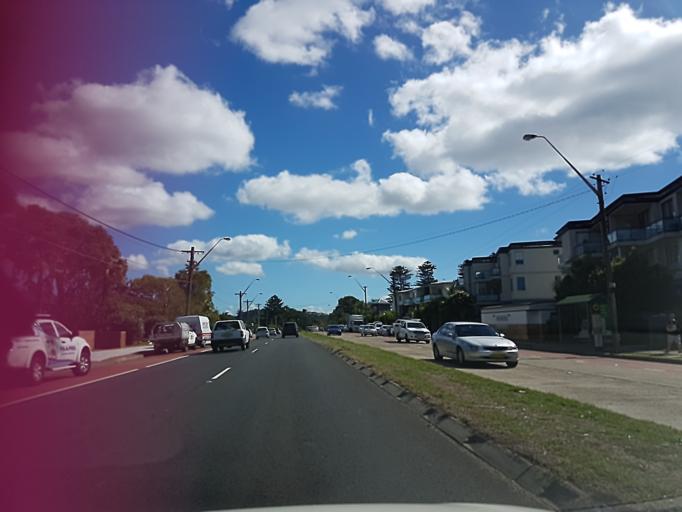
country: AU
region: New South Wales
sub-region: Warringah
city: Narrabeen
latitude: -33.7182
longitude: 151.2977
